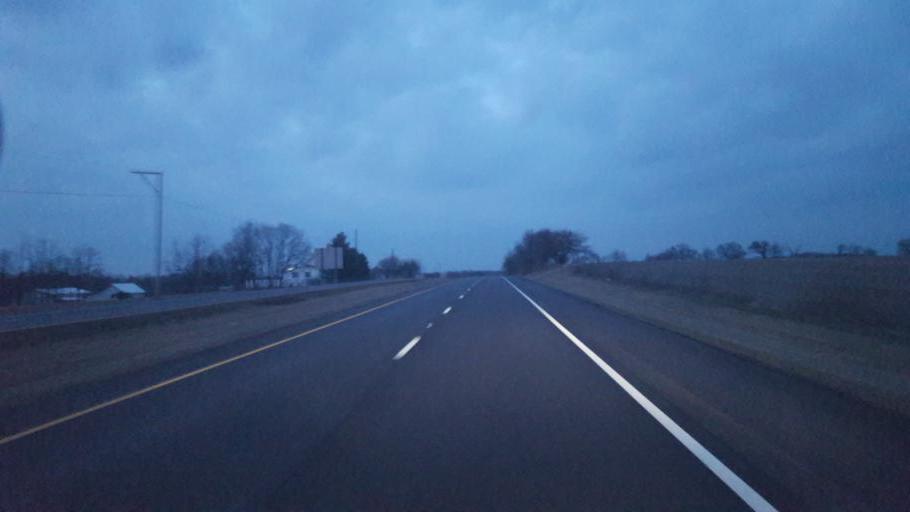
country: US
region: Ohio
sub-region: Ross County
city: Kingston
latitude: 39.4263
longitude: -82.9750
